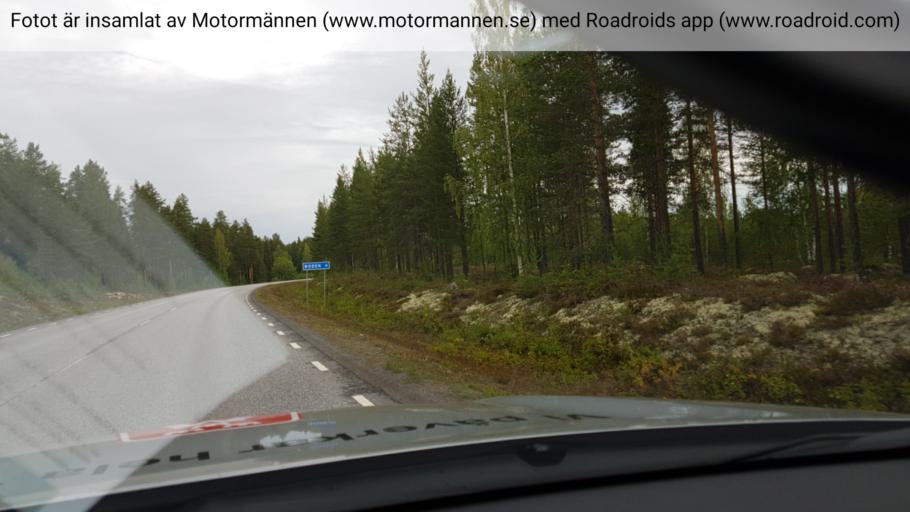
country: SE
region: Norrbotten
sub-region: Bodens Kommun
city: Boden
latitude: 65.7990
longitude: 21.6601
